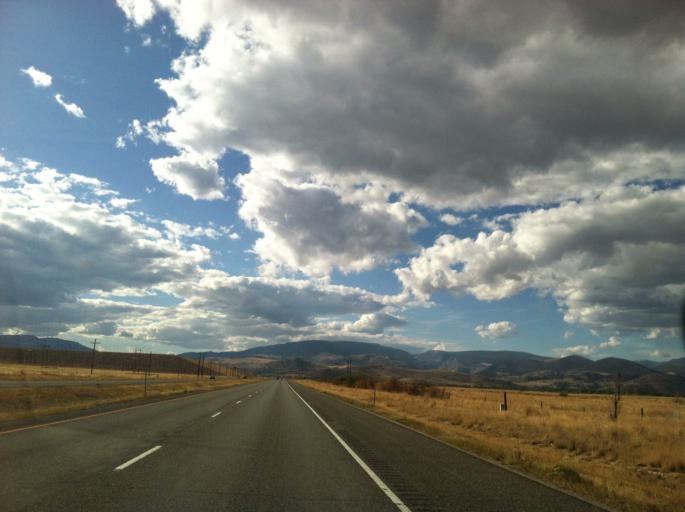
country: US
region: Montana
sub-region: Deer Lodge County
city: Anaconda
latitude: 46.1142
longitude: -112.8641
